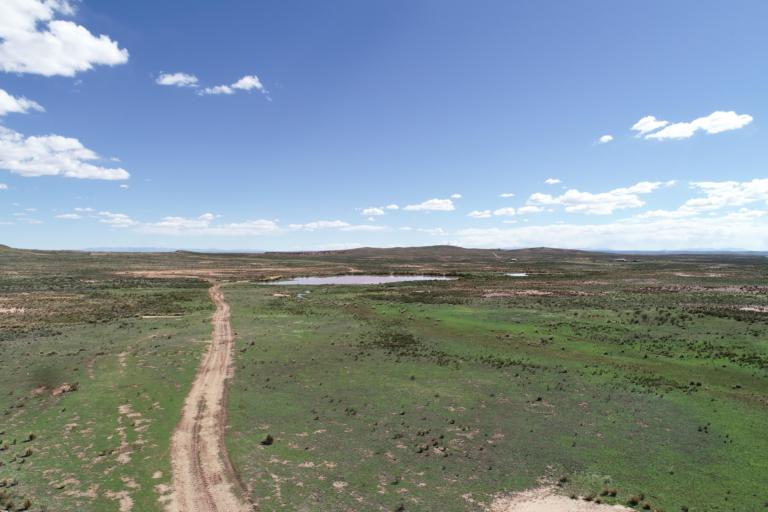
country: BO
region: La Paz
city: Curahuara de Carangas
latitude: -17.2923
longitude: -68.4981
